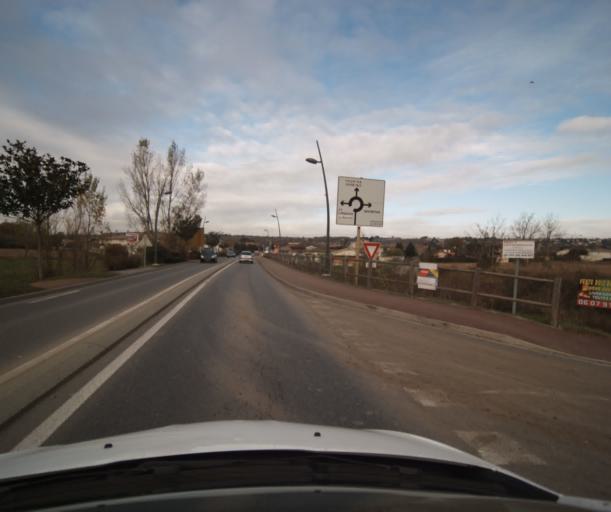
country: FR
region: Midi-Pyrenees
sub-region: Departement de la Haute-Garonne
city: Bruguieres
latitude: 43.7183
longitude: 1.4064
